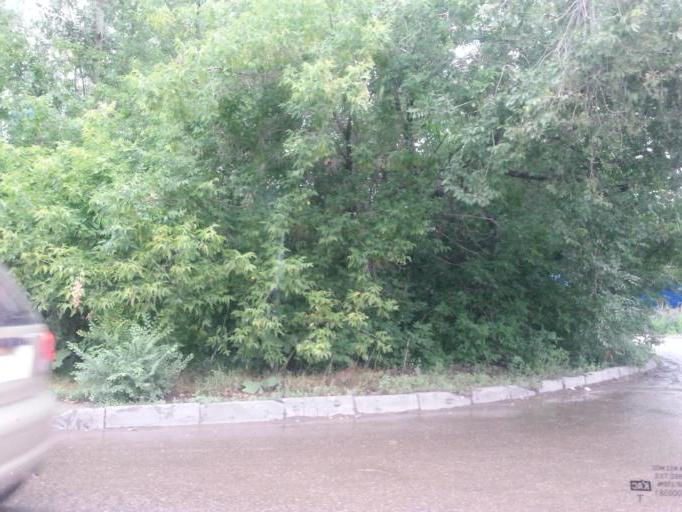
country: RU
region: Tatarstan
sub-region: Gorod Kazan'
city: Kazan
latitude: 55.7628
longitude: 49.1987
